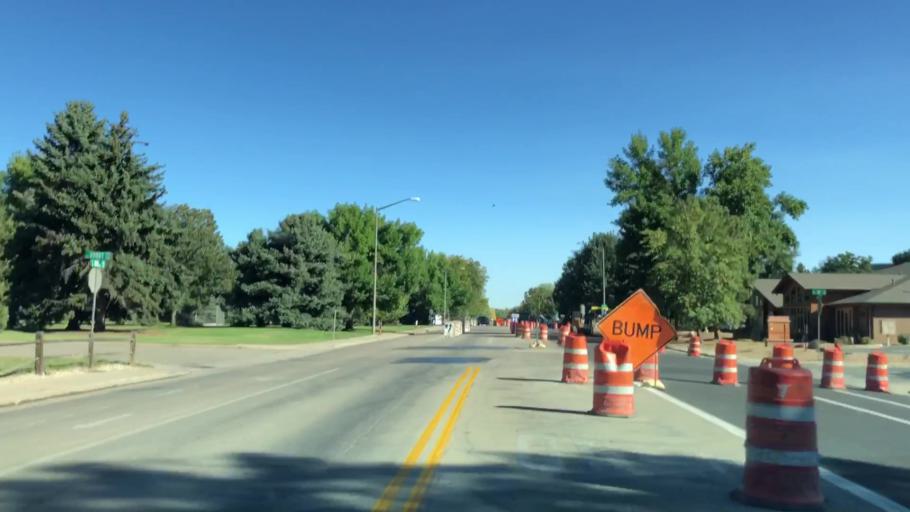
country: US
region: Colorado
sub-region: Larimer County
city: Loveland
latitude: 40.4107
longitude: -105.0537
